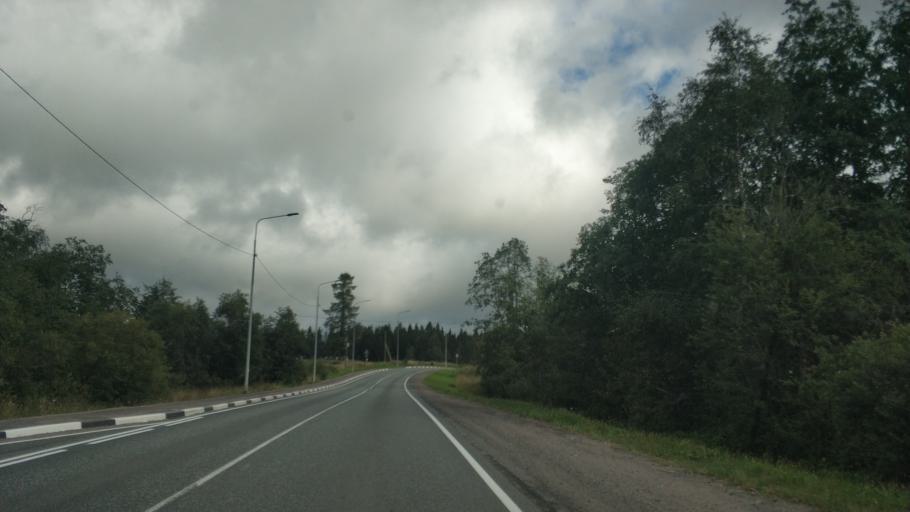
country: RU
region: Republic of Karelia
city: Khelyulya
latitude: 61.7665
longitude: 30.6545
